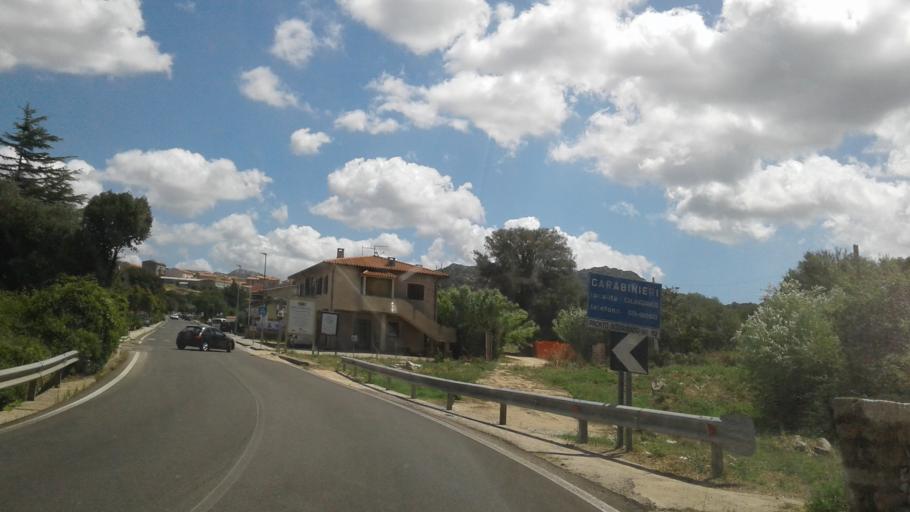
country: IT
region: Sardinia
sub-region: Provincia di Olbia-Tempio
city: Calangianus
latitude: 40.9210
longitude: 9.1824
